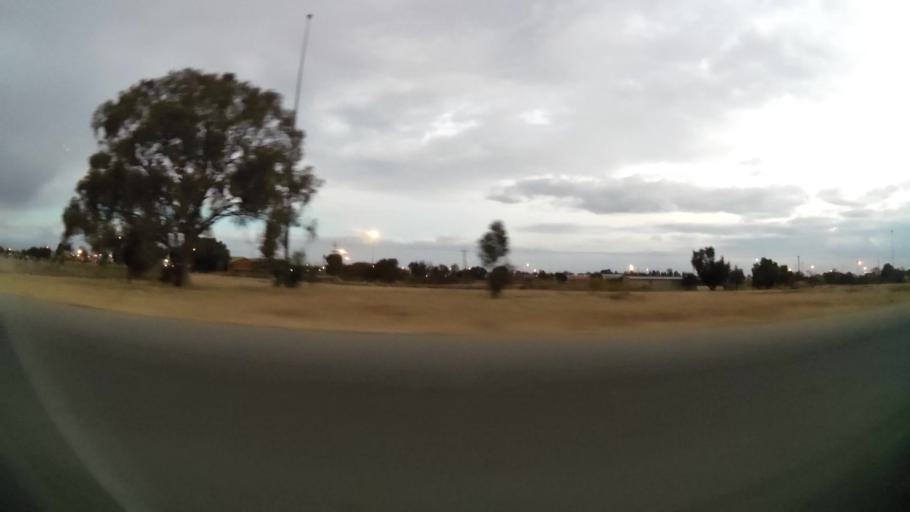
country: ZA
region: Orange Free State
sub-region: Lejweleputswa District Municipality
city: Welkom
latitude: -27.9532
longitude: 26.7891
